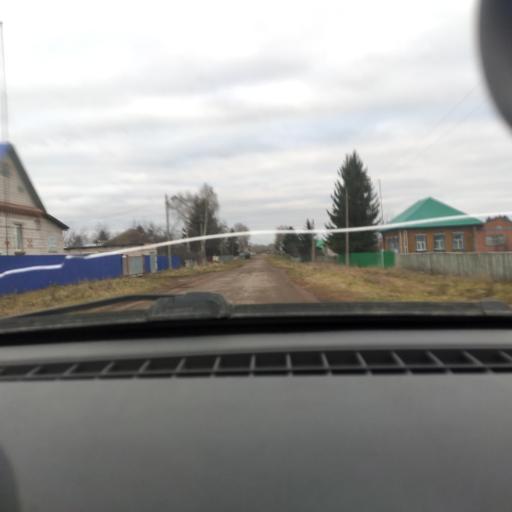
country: RU
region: Bashkortostan
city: Ulukulevo
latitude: 54.4403
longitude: 56.4596
